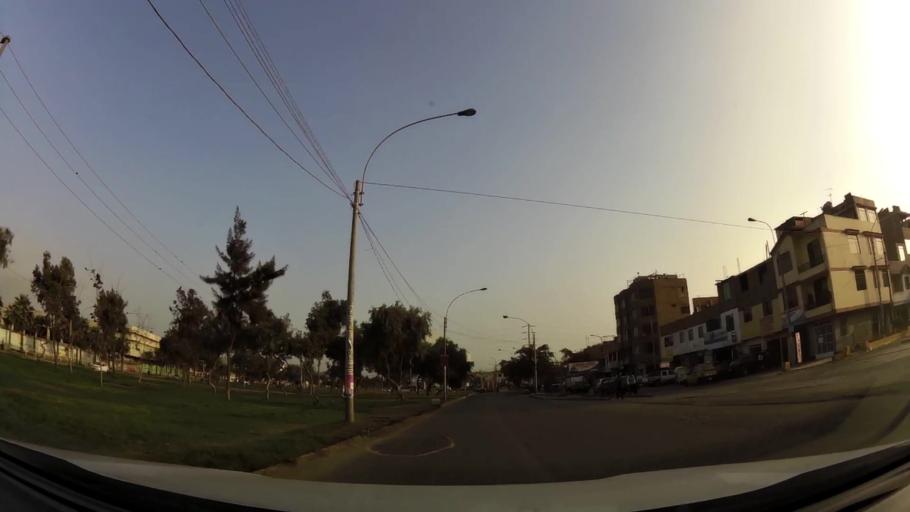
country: PE
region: Lima
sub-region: Lima
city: Independencia
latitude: -11.9763
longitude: -77.0770
